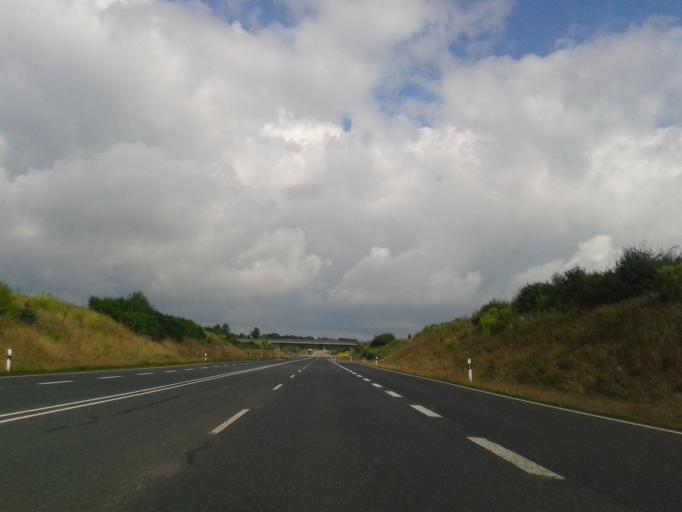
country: DE
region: Saxony
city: Radeberg
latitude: 51.1108
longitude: 13.9357
